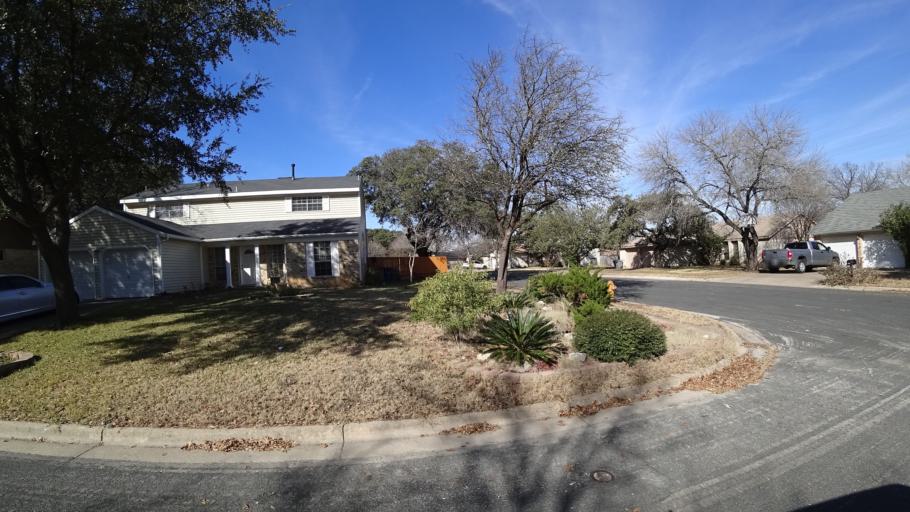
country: US
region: Texas
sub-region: Travis County
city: Wells Branch
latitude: 30.3923
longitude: -97.6912
